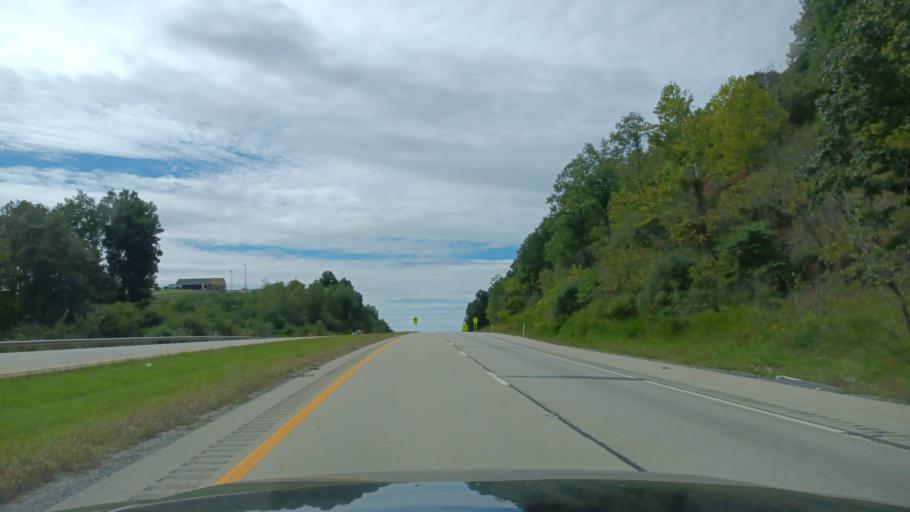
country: US
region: West Virginia
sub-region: Doddridge County
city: West Union
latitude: 39.2793
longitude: -80.7802
